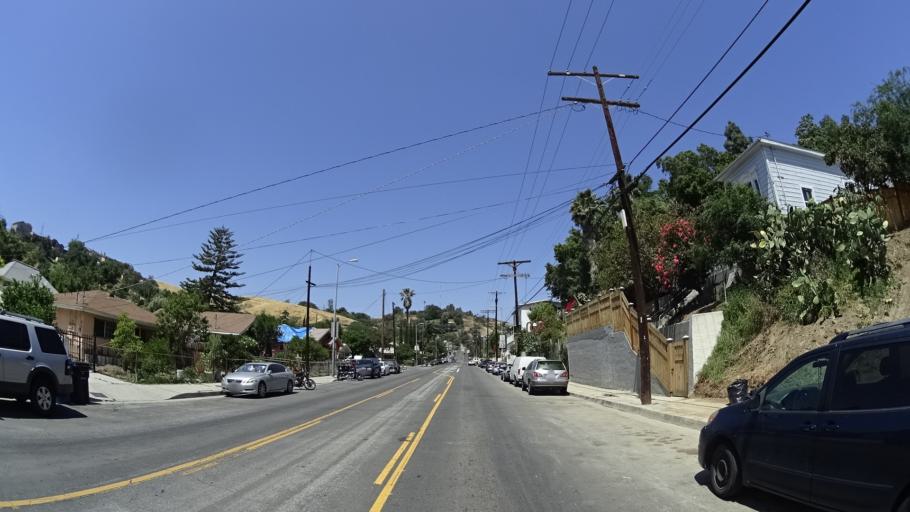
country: US
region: California
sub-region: Los Angeles County
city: Boyle Heights
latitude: 34.0765
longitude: -118.2027
